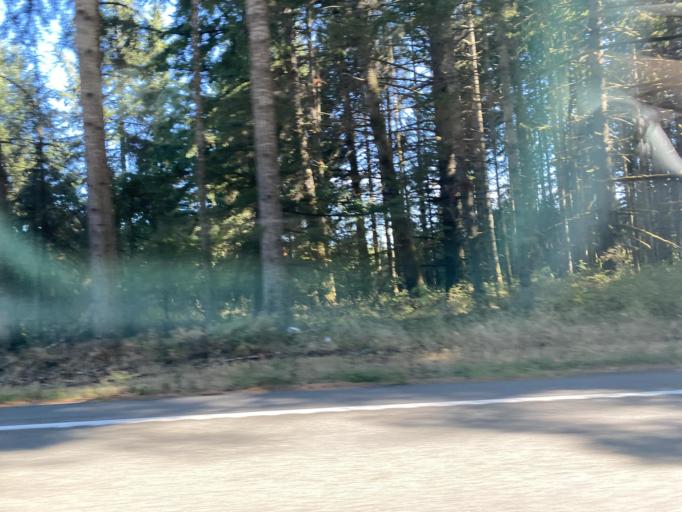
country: US
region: Washington
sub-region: Thurston County
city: Rainier
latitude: 46.9190
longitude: -122.7444
